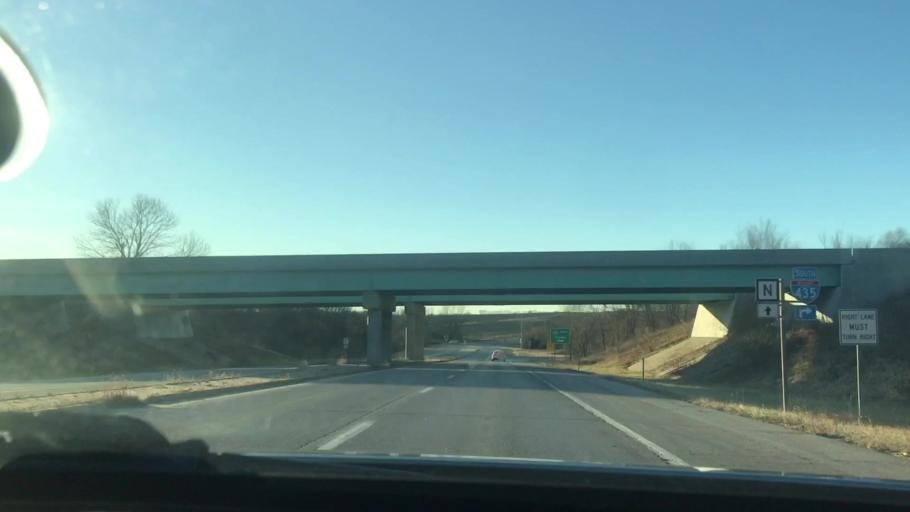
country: US
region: Missouri
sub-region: Platte County
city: Weatherby Lake
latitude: 39.2454
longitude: -94.7544
